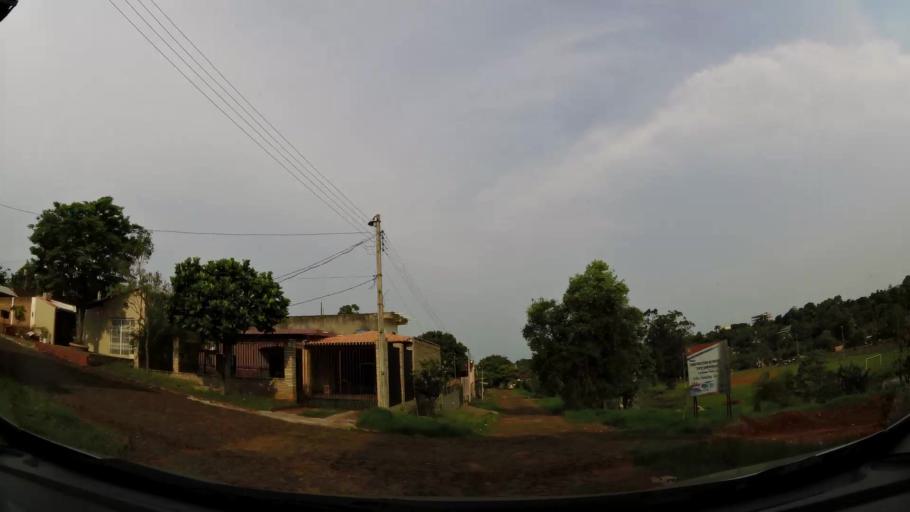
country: PY
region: Alto Parana
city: Ciudad del Este
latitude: -25.4929
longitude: -54.6568
